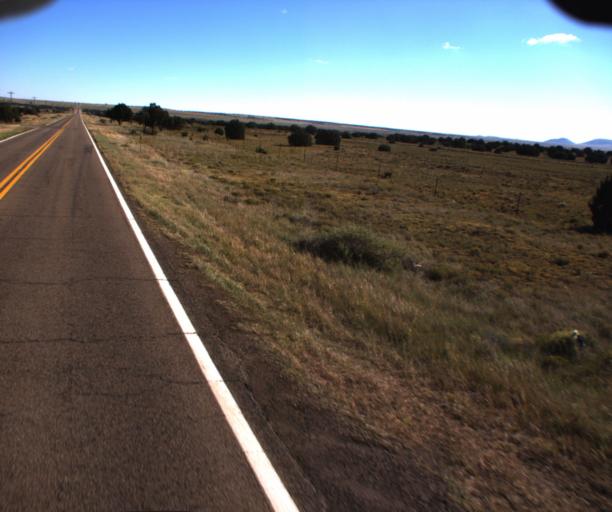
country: US
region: Arizona
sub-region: Navajo County
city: White Mountain Lake
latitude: 34.3373
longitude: -109.7373
